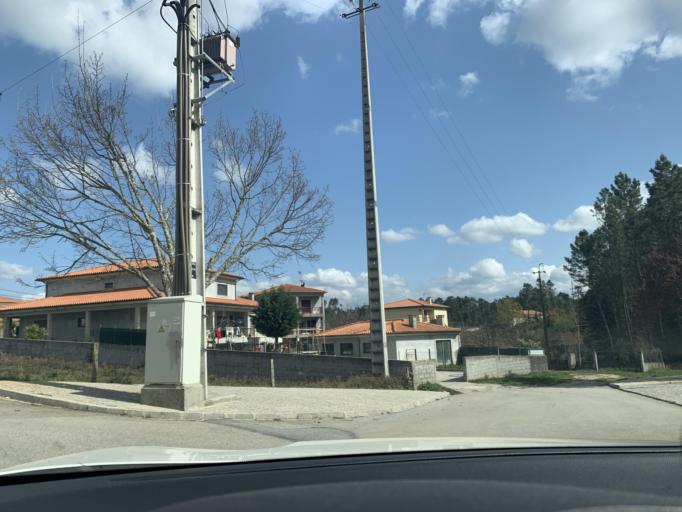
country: PT
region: Viseu
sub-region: Viseu
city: Rio de Loba
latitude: 40.6975
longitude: -7.8609
